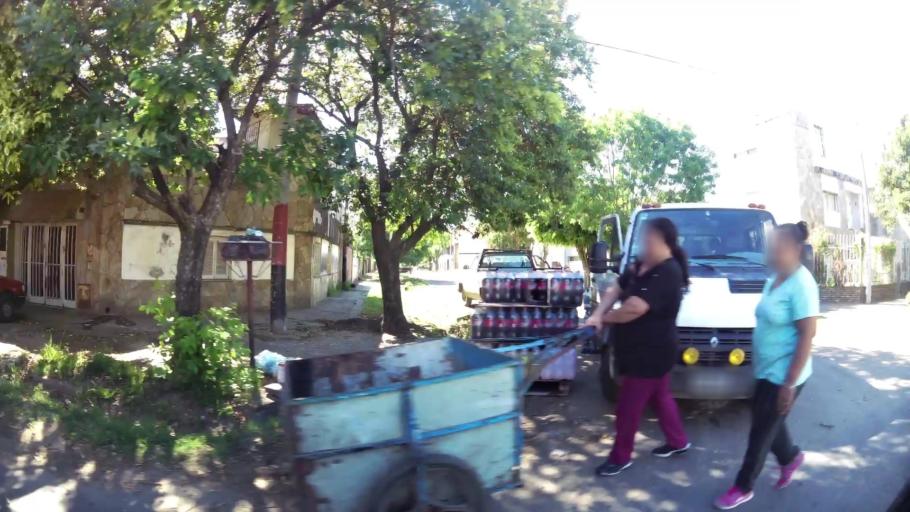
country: AR
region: Santa Fe
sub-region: Departamento de Rosario
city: Rosario
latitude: -32.9565
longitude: -60.6892
